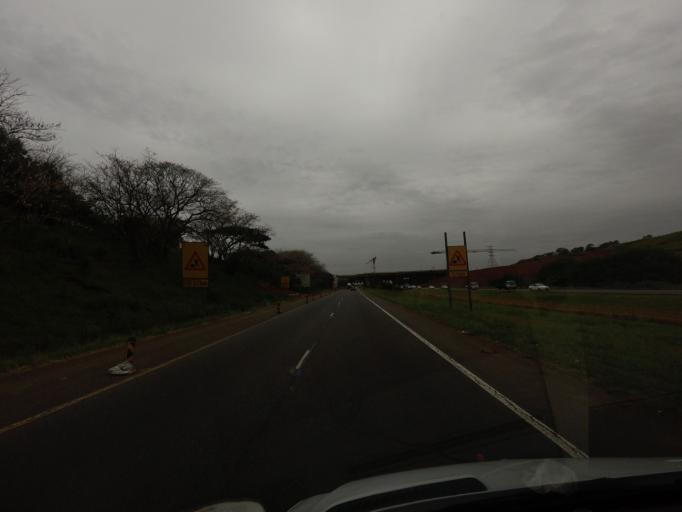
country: ZA
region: KwaZulu-Natal
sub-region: eThekwini Metropolitan Municipality
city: Durban
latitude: -29.7127
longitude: 31.0652
